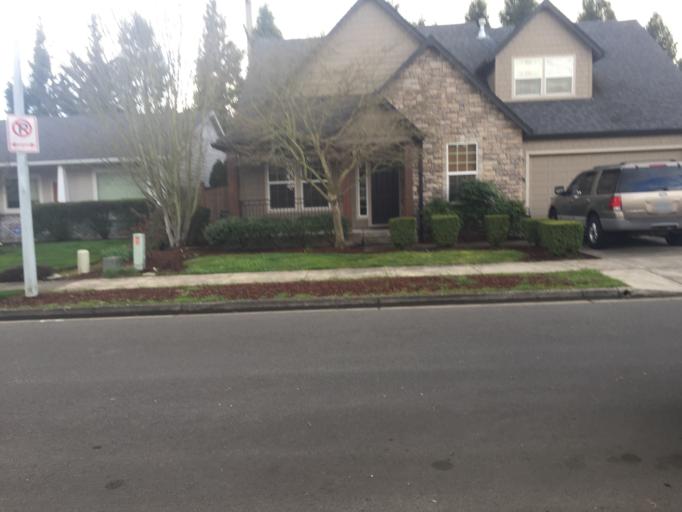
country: US
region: Oregon
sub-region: Lane County
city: Eugene
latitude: 44.1002
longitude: -123.1560
